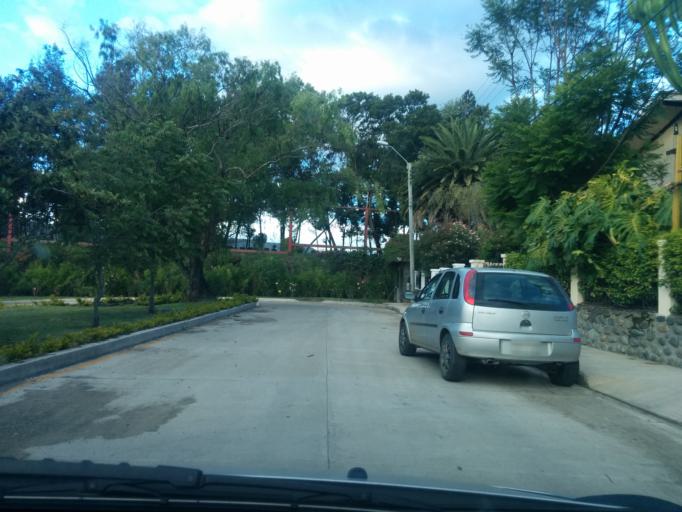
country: EC
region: Azuay
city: Llacao
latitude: -2.8771
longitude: -78.9449
